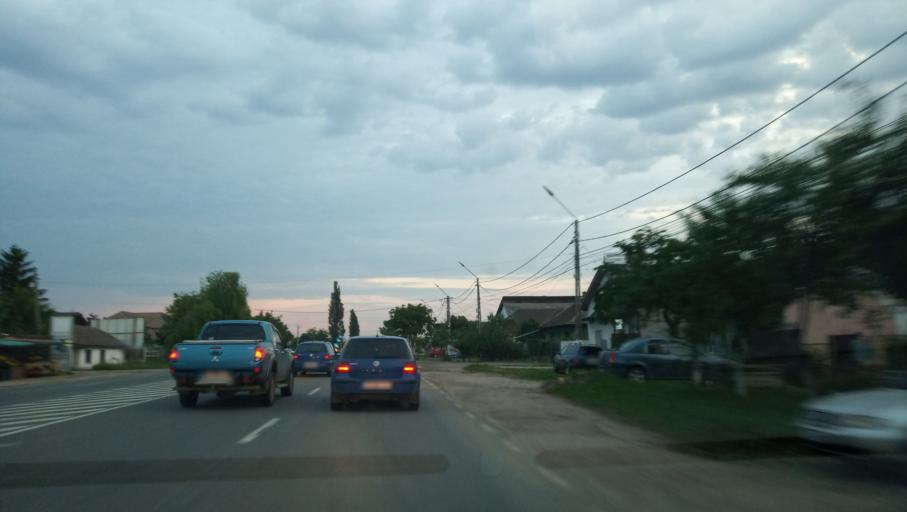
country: RO
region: Timis
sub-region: Comuna Sag
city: Sag
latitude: 45.6552
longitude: 21.1739
